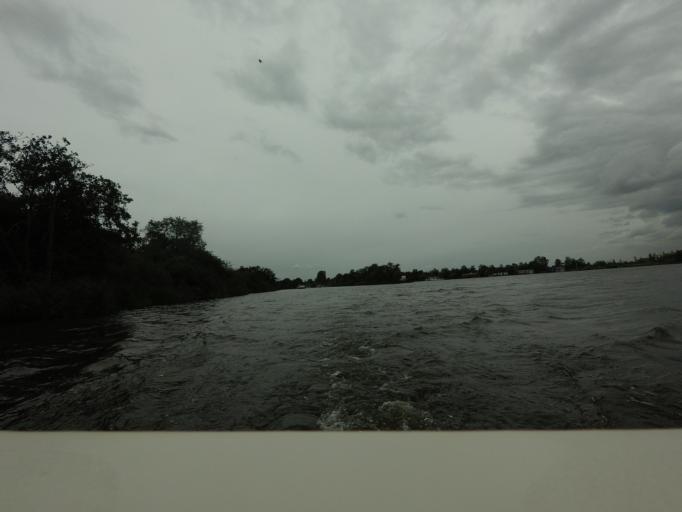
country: NL
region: Friesland
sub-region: Gemeente Tytsjerksteradiel
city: Garyp
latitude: 53.1194
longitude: 5.9440
